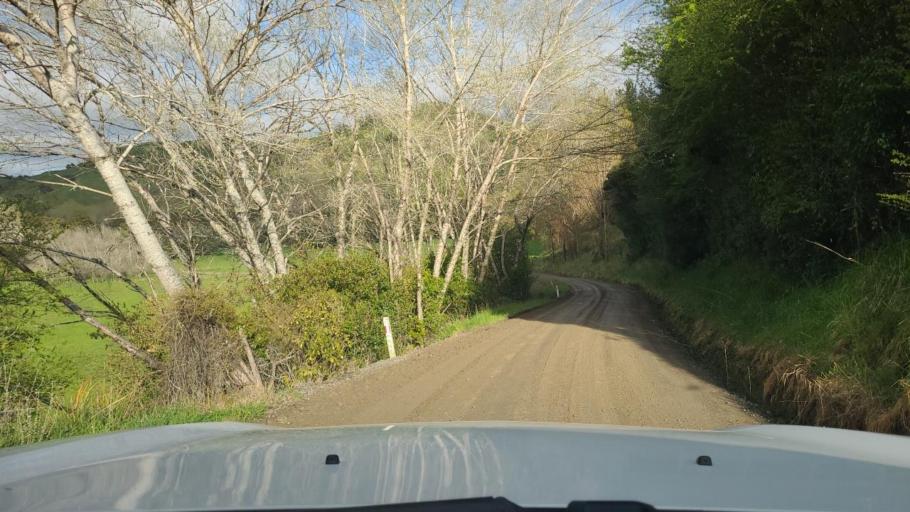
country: NZ
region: Wellington
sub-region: South Wairarapa District
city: Waipawa
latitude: -41.2231
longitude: 175.6842
